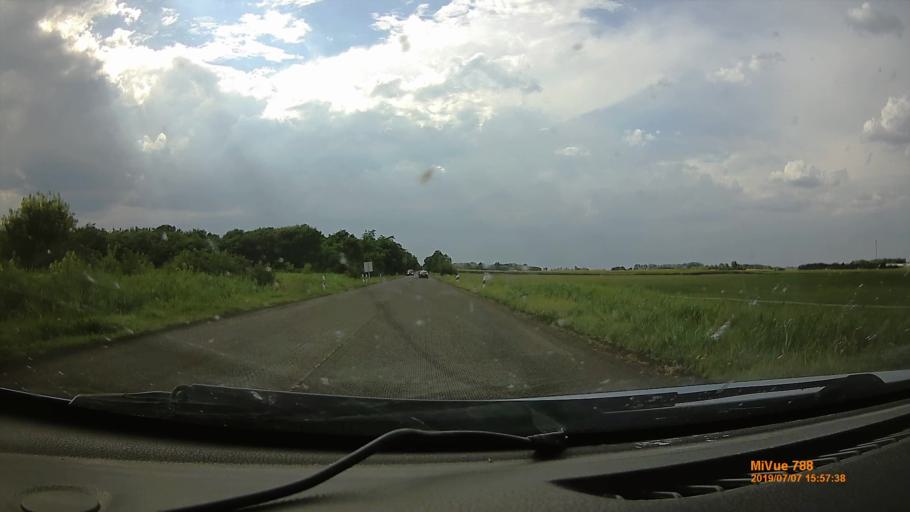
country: HU
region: Pest
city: Szentlorinckata
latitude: 47.5776
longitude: 19.7592
